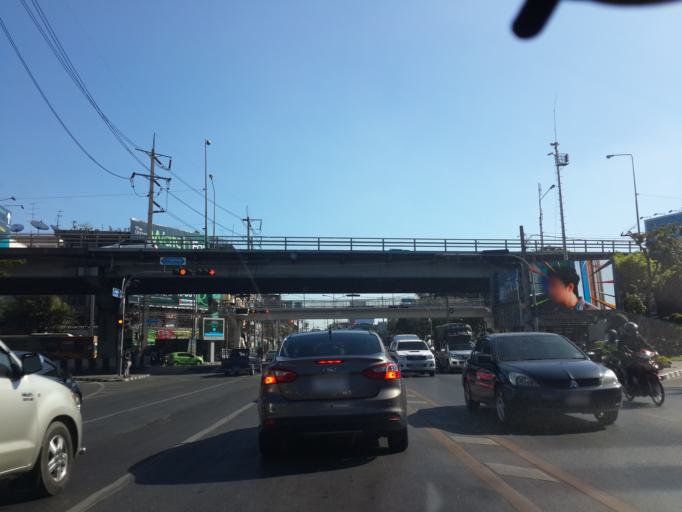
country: TH
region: Bangkok
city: Bang Kapi
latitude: 13.7632
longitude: 100.6457
